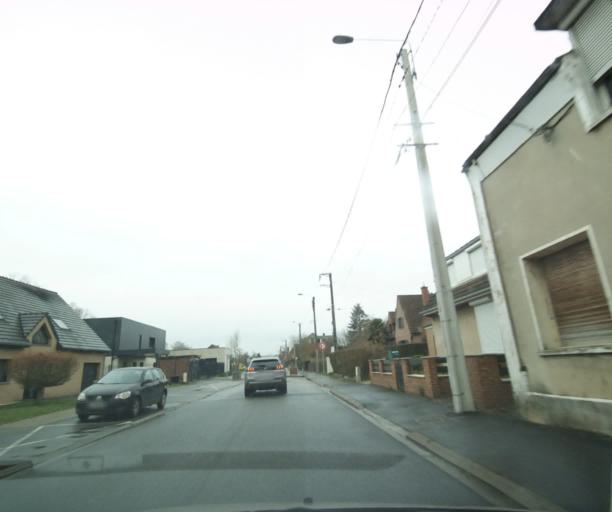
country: FR
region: Nord-Pas-de-Calais
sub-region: Departement du Nord
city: Prouvy
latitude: 50.3218
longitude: 3.4445
